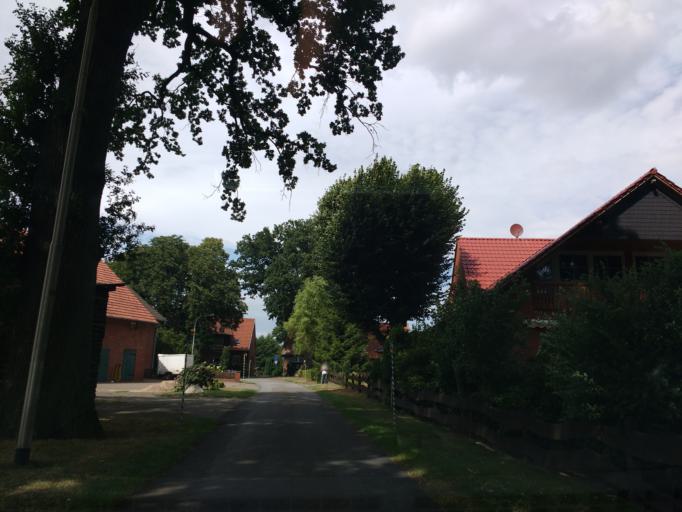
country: DE
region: Lower Saxony
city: Wiedensahl
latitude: 52.4362
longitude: 9.0671
